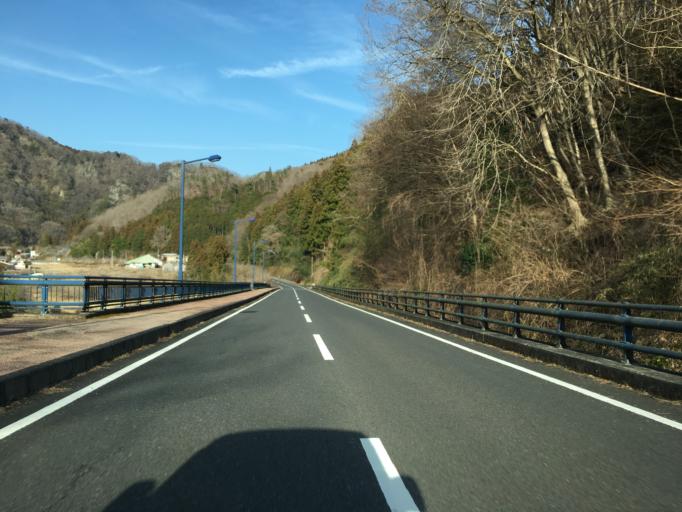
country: JP
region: Ibaraki
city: Daigo
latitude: 36.7580
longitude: 140.3947
